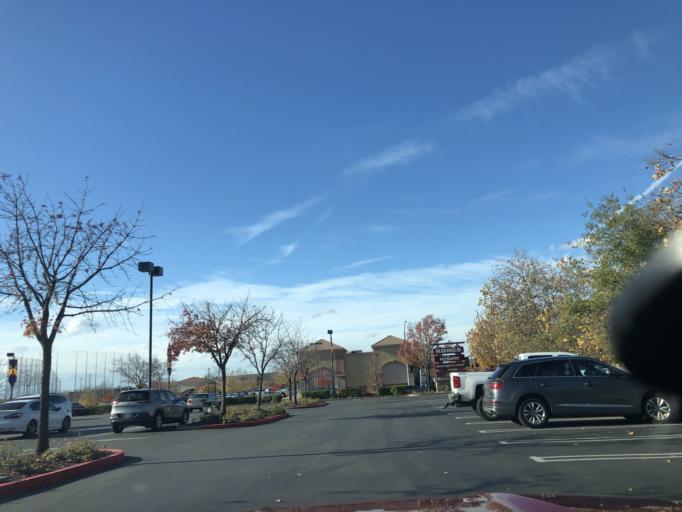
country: US
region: California
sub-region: Placer County
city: Roseville
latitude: 38.7900
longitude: -121.2862
